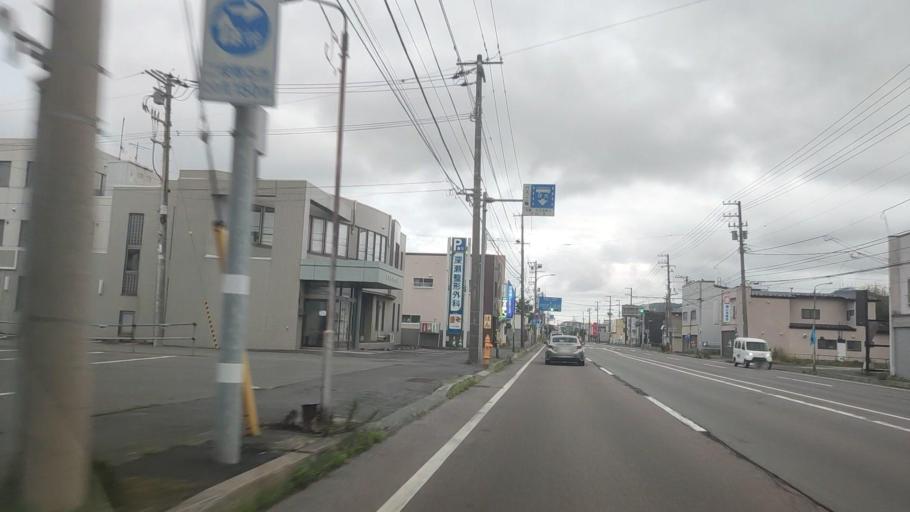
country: JP
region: Hokkaido
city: Hakodate
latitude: 41.7918
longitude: 140.7326
